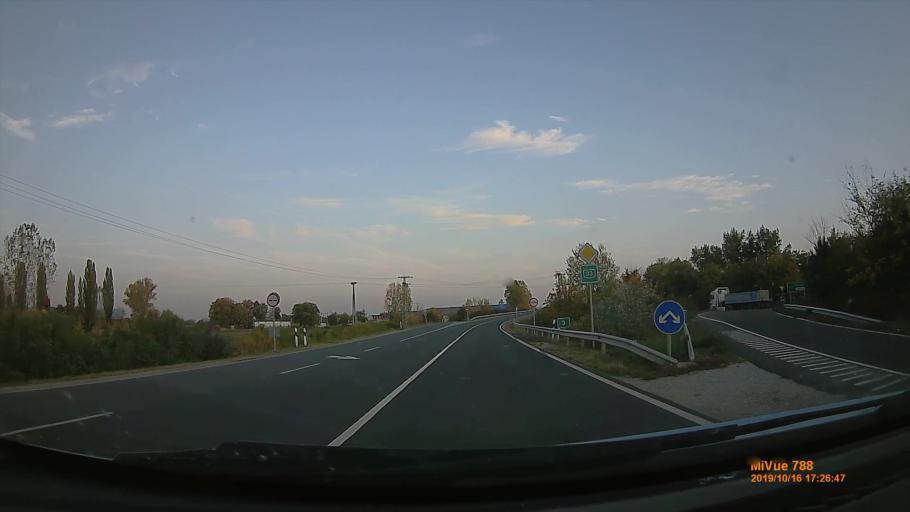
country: HU
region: Heves
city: Fuzesabony
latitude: 47.7409
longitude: 20.4054
